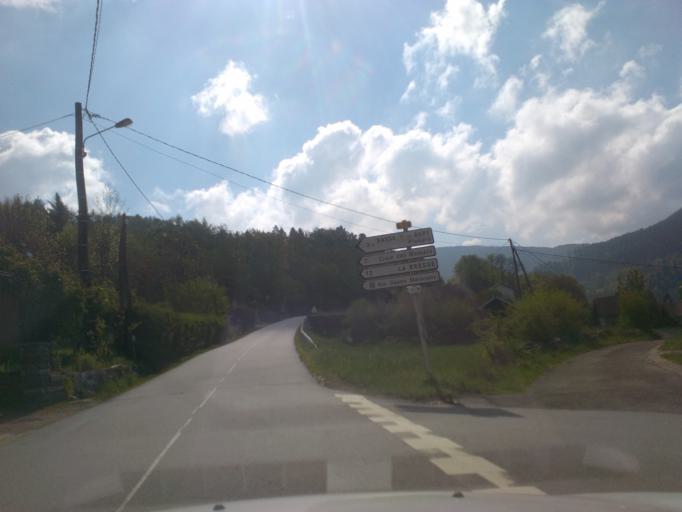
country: FR
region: Lorraine
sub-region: Departement des Vosges
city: Vagney
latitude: 47.9951
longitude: 6.7339
